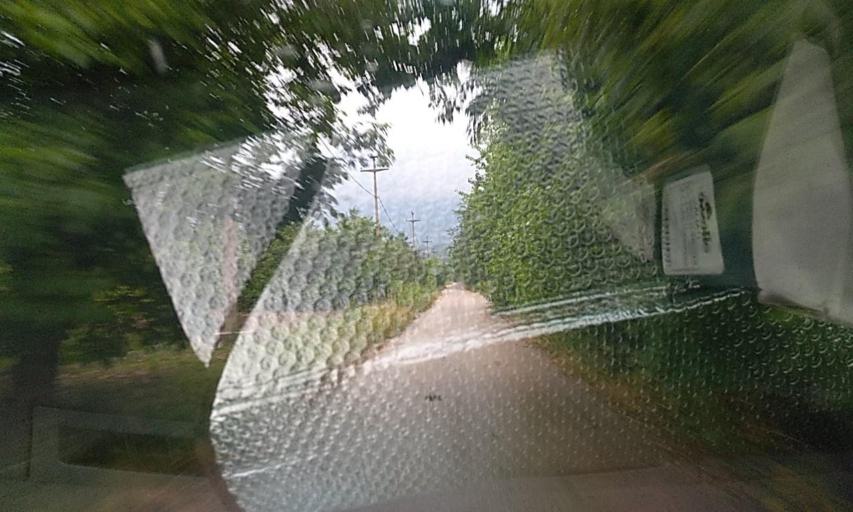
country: RS
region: Central Serbia
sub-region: Pirotski Okrug
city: Bela Palanka
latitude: 43.2504
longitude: 22.1940
